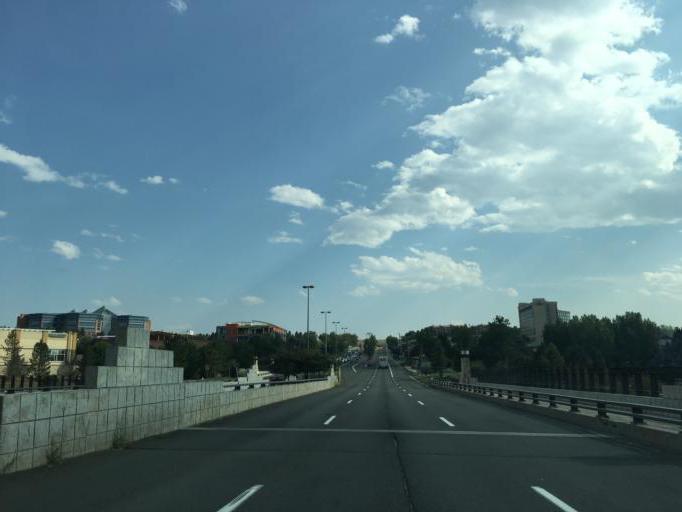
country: US
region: Colorado
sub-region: Broomfield County
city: Broomfield
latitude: 39.9313
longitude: -105.1279
